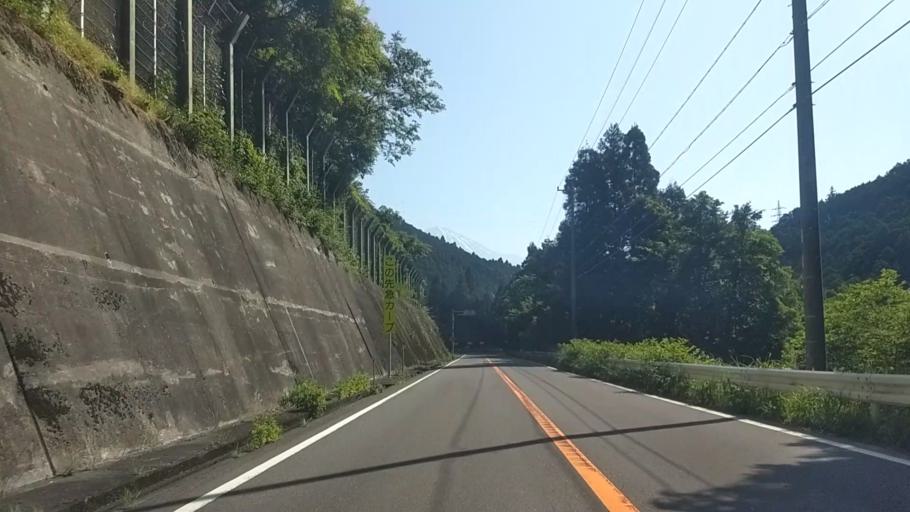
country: JP
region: Shizuoka
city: Fujinomiya
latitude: 35.1936
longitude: 138.5310
